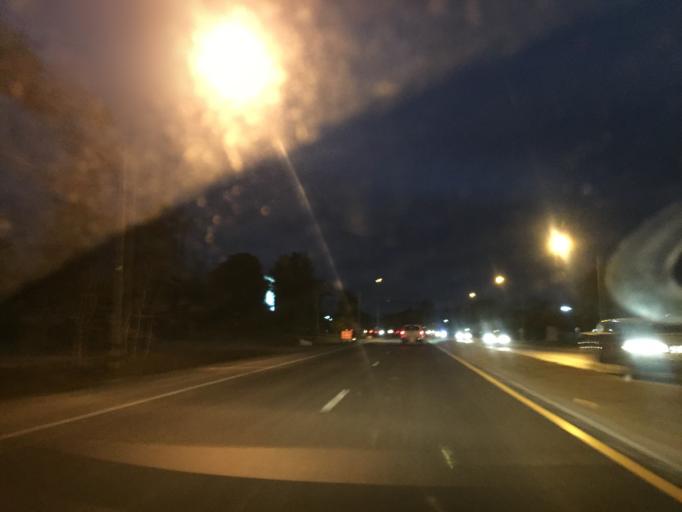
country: TH
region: Changwat Nong Bua Lamphu
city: Na Klang
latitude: 17.2965
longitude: 102.2128
